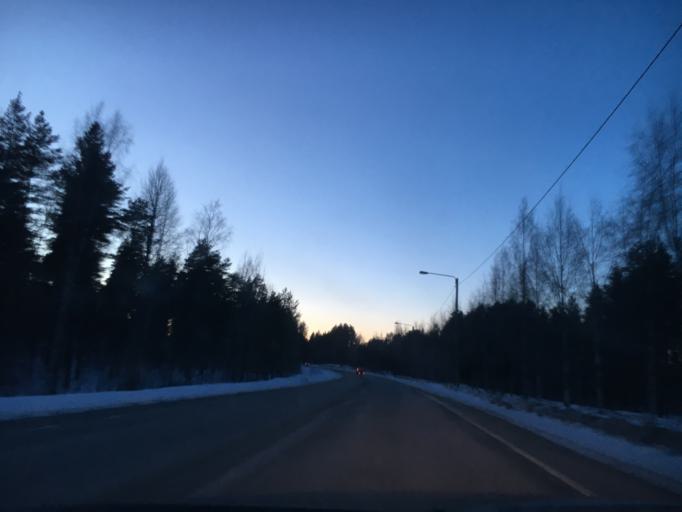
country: FI
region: Kainuu
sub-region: Kajaani
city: Kajaani
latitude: 64.2015
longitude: 27.7453
